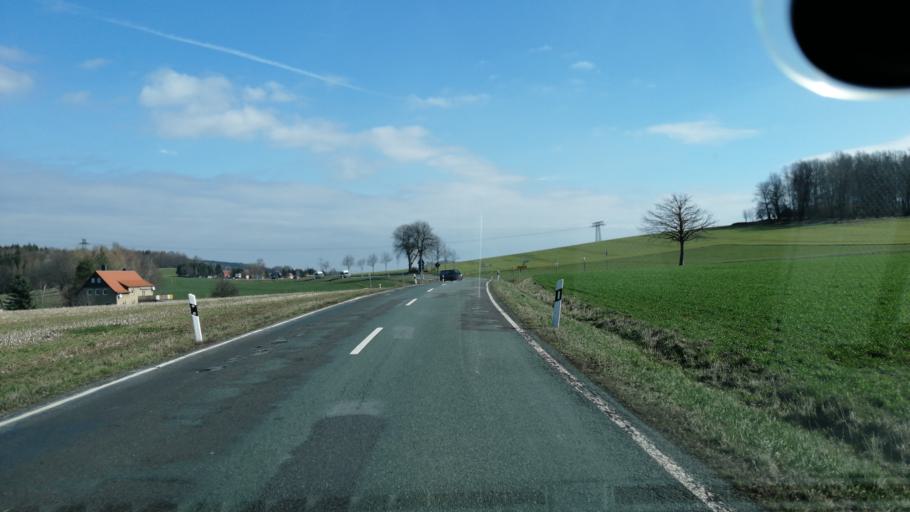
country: DE
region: Saxony
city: Schonbach
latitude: 51.0792
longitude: 14.5566
